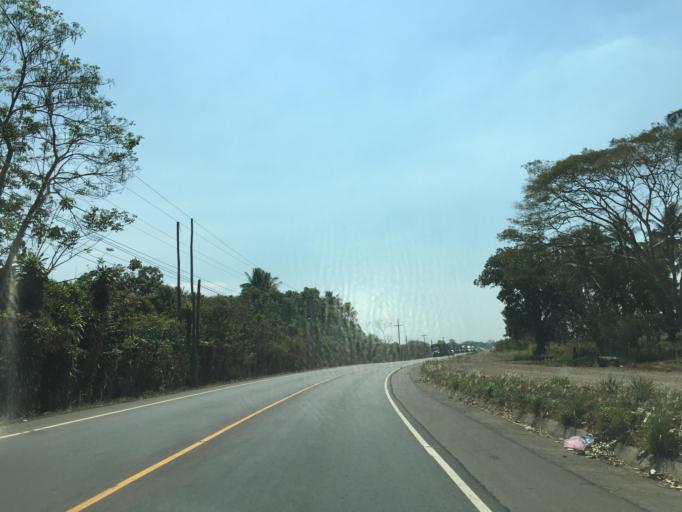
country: GT
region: Escuintla
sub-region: Municipio de Escuintla
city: Escuintla
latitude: 14.2710
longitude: -90.7545
